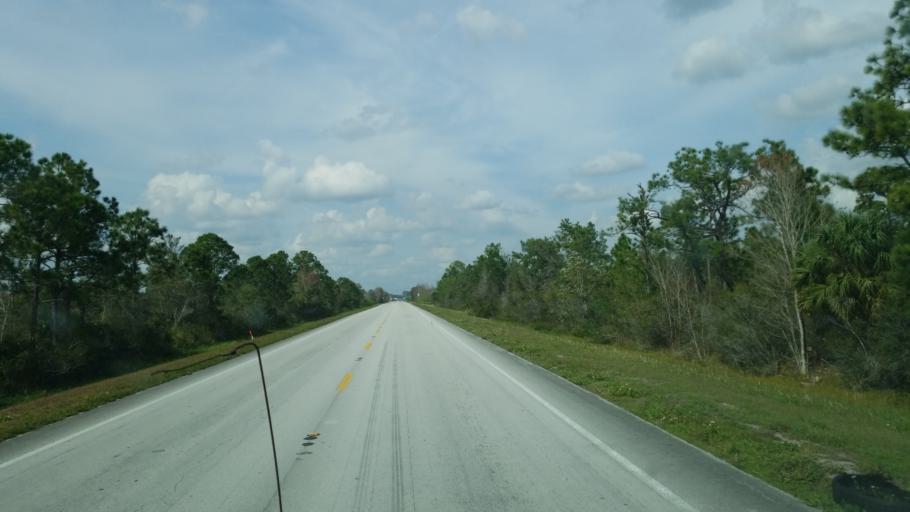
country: US
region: Florida
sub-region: Indian River County
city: Fellsmere
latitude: 27.6922
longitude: -80.9004
